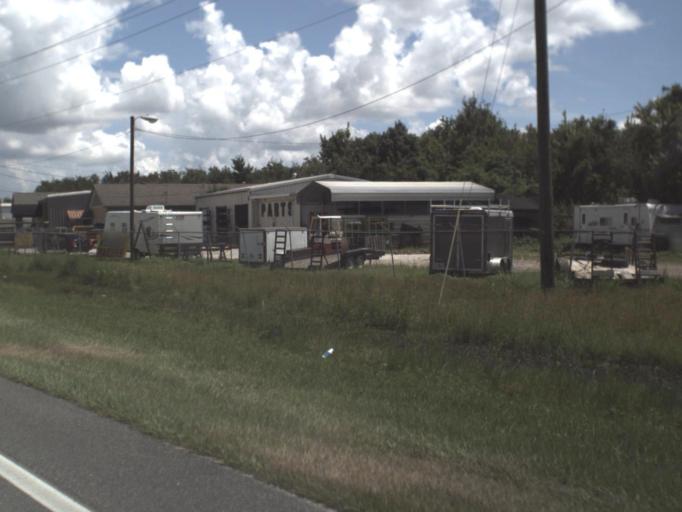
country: US
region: Florida
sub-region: Polk County
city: Fussels Corner
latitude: 28.0555
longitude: -81.8297
